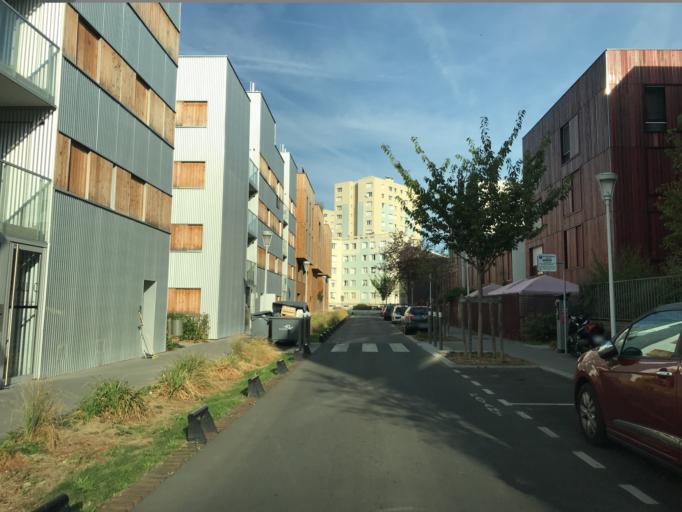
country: FR
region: Ile-de-France
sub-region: Departement des Hauts-de-Seine
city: Nanterre
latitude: 48.9006
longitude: 2.1982
